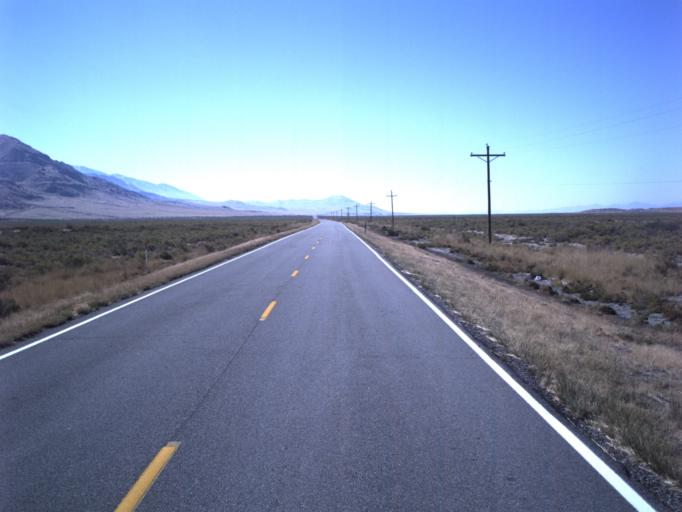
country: US
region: Utah
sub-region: Tooele County
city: Grantsville
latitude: 40.7368
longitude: -112.6557
